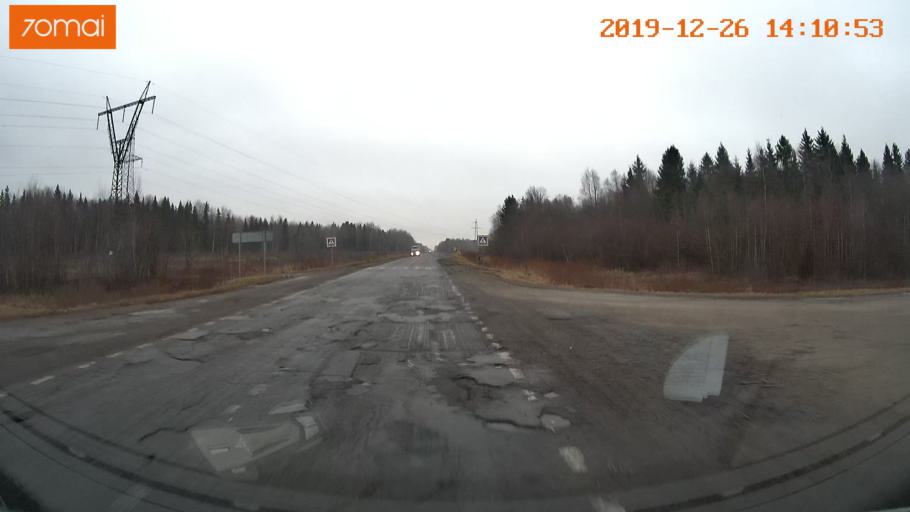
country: RU
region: Jaroslavl
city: Poshekhon'ye
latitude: 58.5088
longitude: 38.9628
